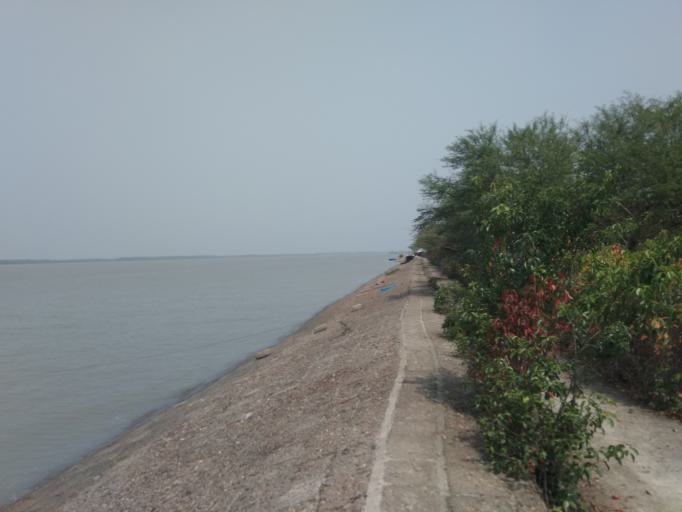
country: IN
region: West Bengal
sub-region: North 24 Parganas
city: Gosaba
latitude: 22.2529
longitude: 89.2504
